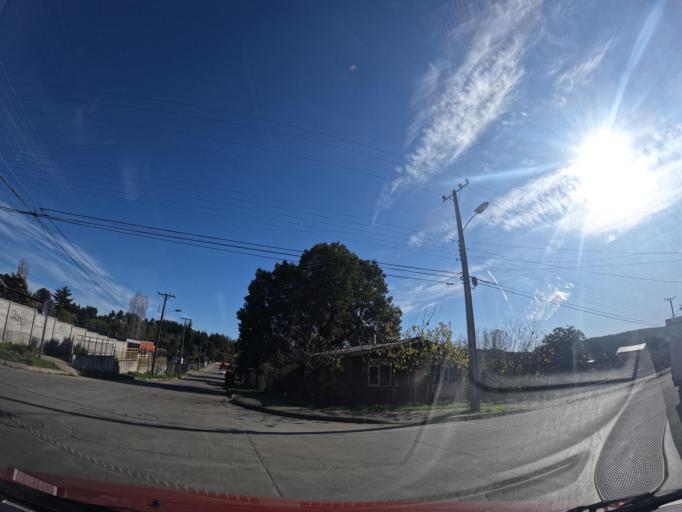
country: CL
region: Biobio
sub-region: Provincia de Biobio
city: Yumbel
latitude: -36.8260
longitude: -72.6648
